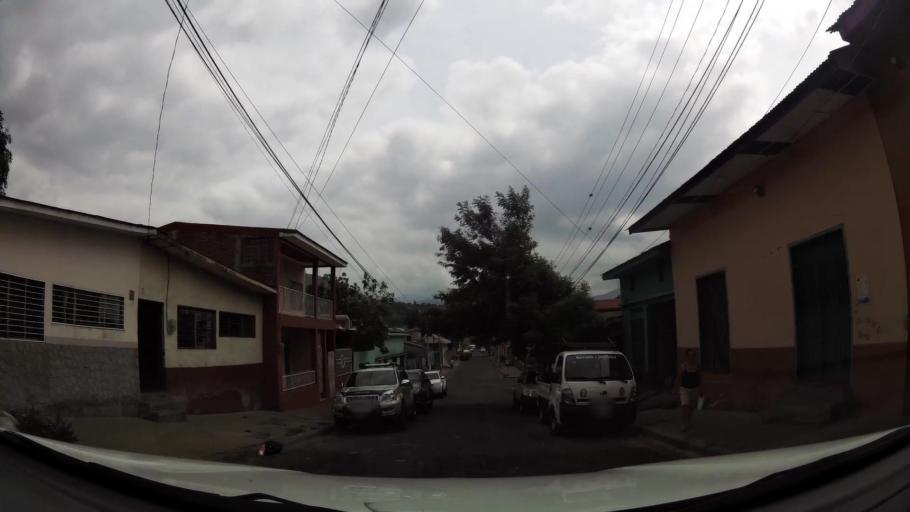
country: NI
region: Matagalpa
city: Matagalpa
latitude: 12.9191
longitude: -85.9236
